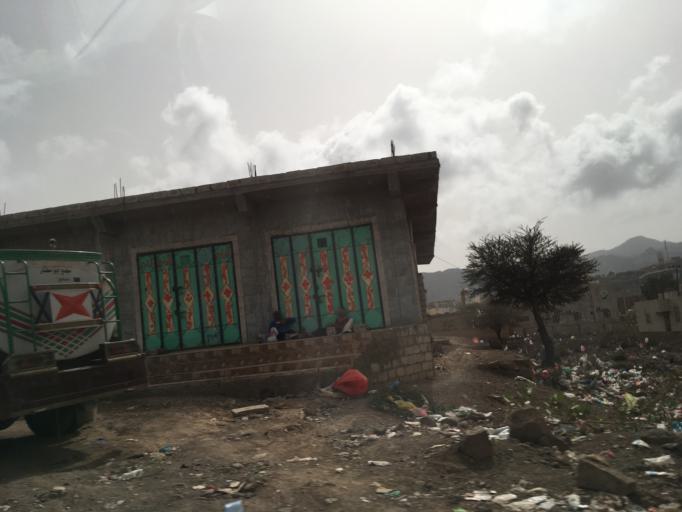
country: YE
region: Ad Dali'
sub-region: Ad Dhale'e
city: Dhalie
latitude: 13.7036
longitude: 44.7375
